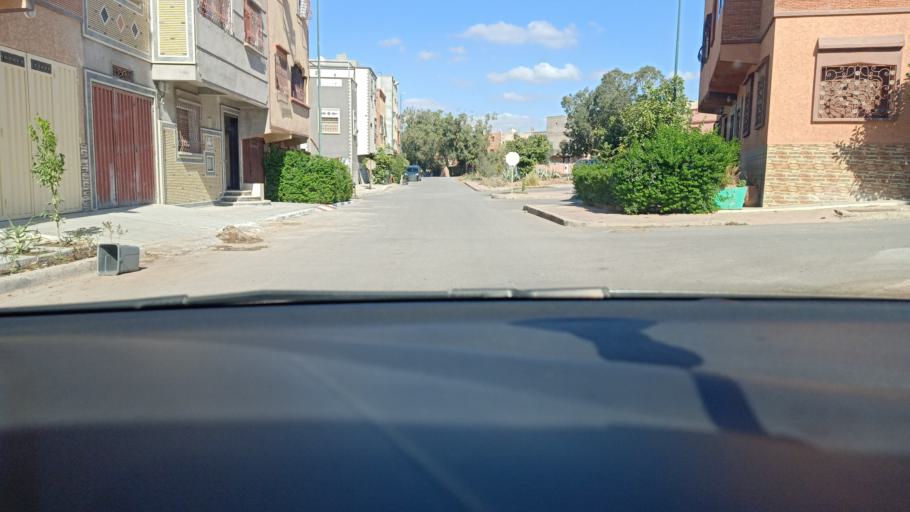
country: MA
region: Doukkala-Abda
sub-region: Safi
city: Youssoufia
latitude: 32.2392
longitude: -8.5310
